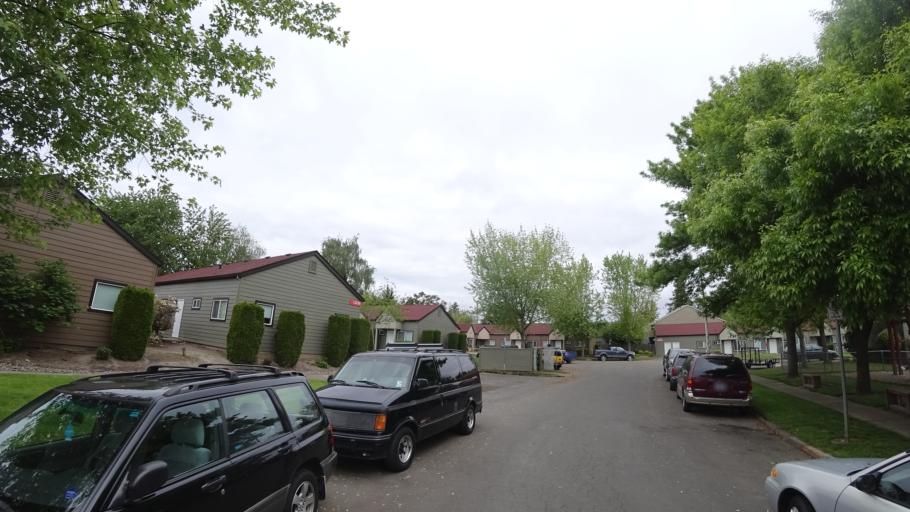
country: US
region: Oregon
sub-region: Washington County
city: Beaverton
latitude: 45.4751
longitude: -122.8024
